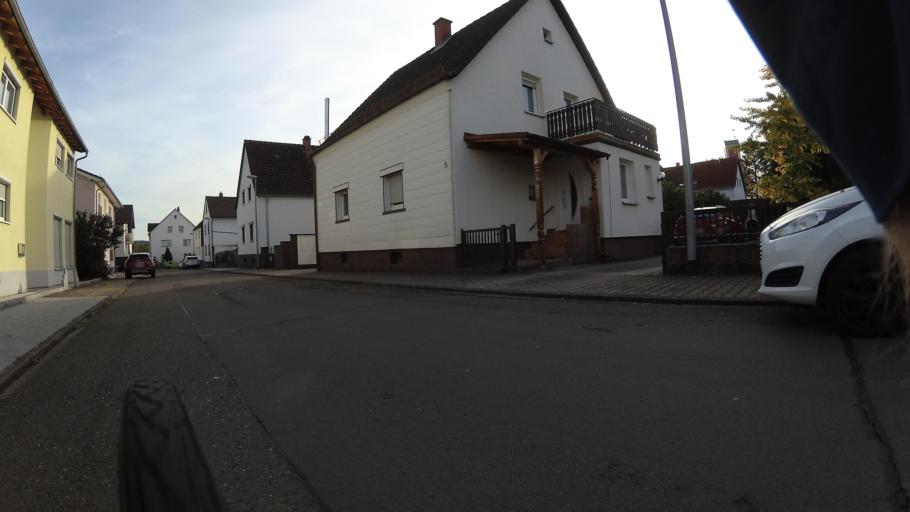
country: DE
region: Rheinland-Pfalz
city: Ramstein-Miesenbach
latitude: 49.4420
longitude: 7.5523
